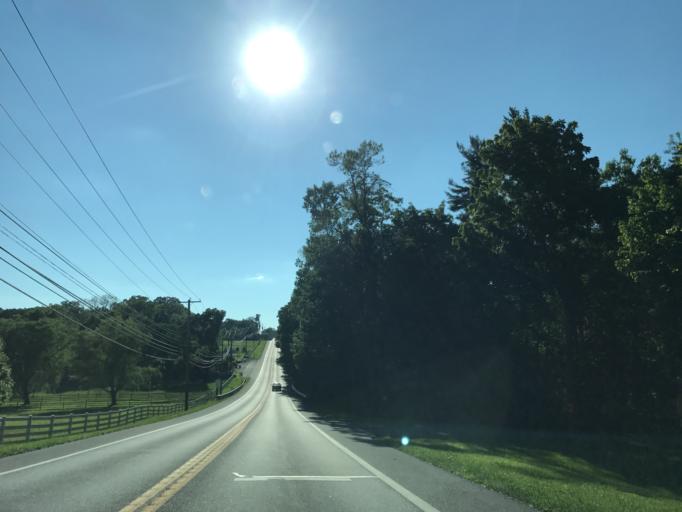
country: US
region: Pennsylvania
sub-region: Lancaster County
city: Elizabethtown
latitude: 40.1586
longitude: -76.6173
